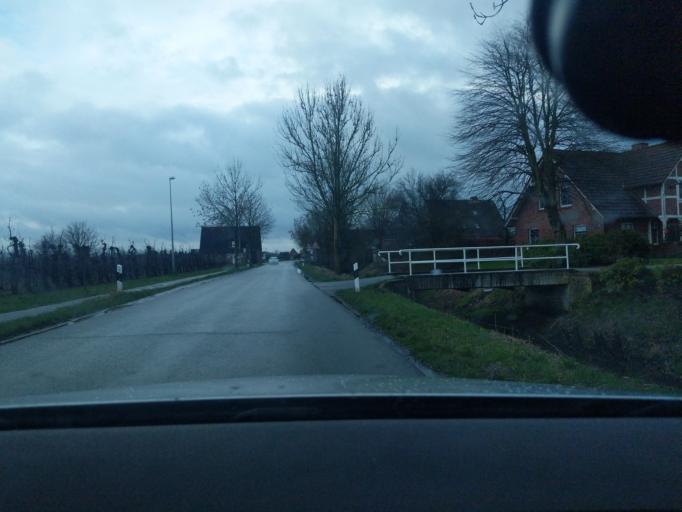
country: DE
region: Lower Saxony
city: Jork
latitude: 53.5368
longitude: 9.6540
